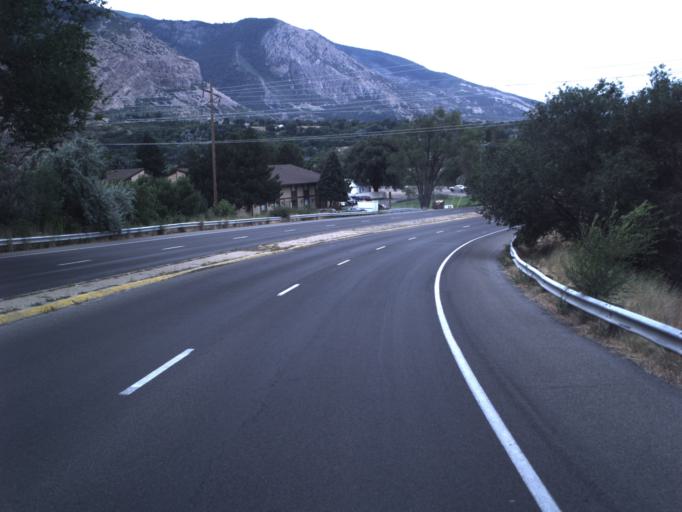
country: US
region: Utah
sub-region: Weber County
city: Ogden
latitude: 41.2439
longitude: -111.9457
